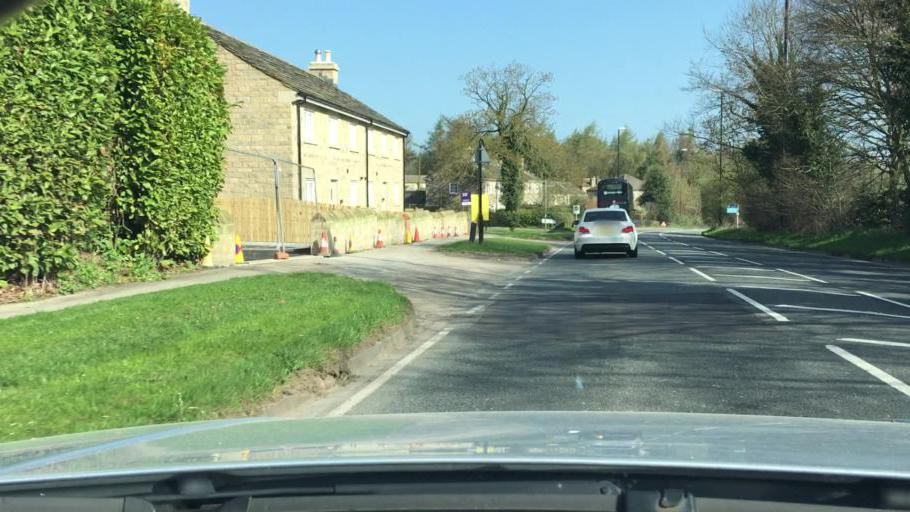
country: GB
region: England
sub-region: City and Borough of Leeds
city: East Keswick
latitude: 53.9028
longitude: -1.5119
